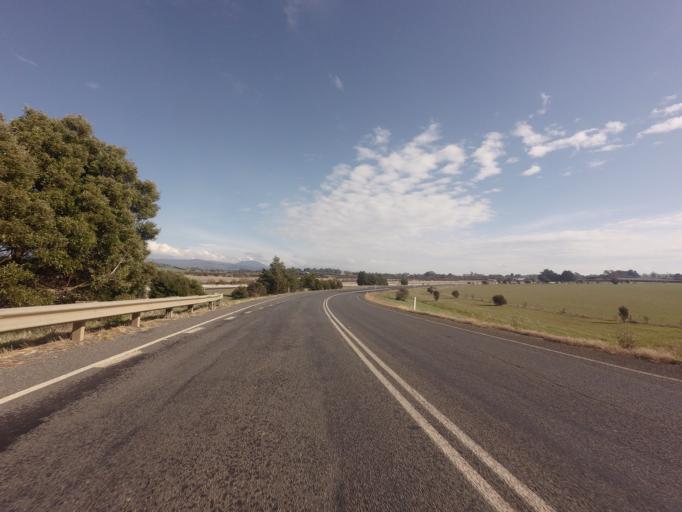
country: AU
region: Tasmania
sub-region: Meander Valley
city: Westbury
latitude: -41.5281
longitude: 146.8723
